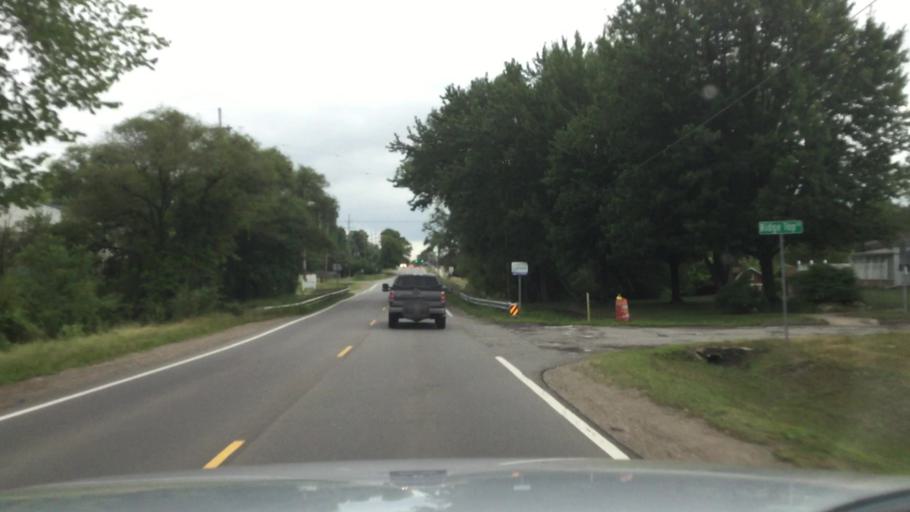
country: US
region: Michigan
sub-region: Oakland County
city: Waterford
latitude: 42.6653
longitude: -83.3865
